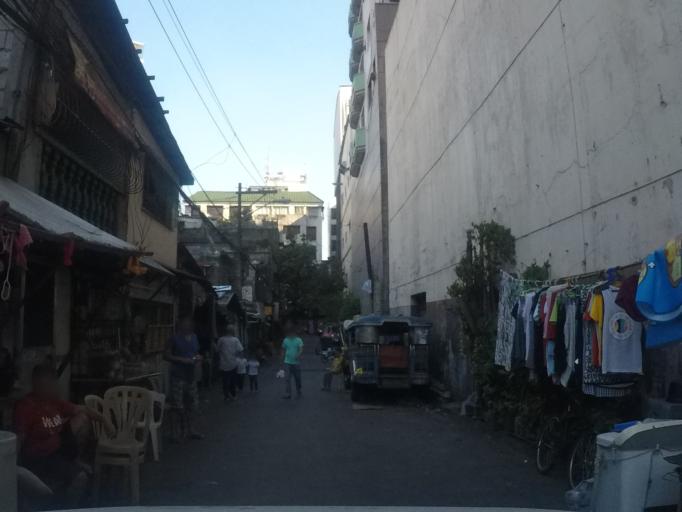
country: PH
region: Metro Manila
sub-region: San Juan
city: San Juan
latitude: 14.6045
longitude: 121.0502
